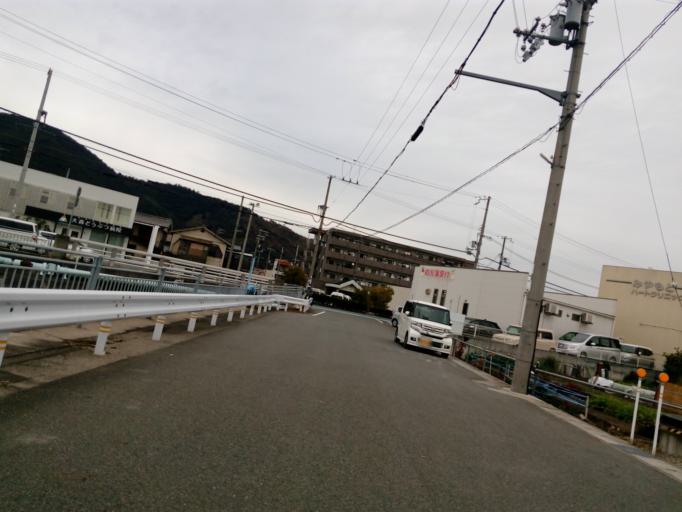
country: JP
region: Hyogo
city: Himeji
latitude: 34.8071
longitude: 134.6162
